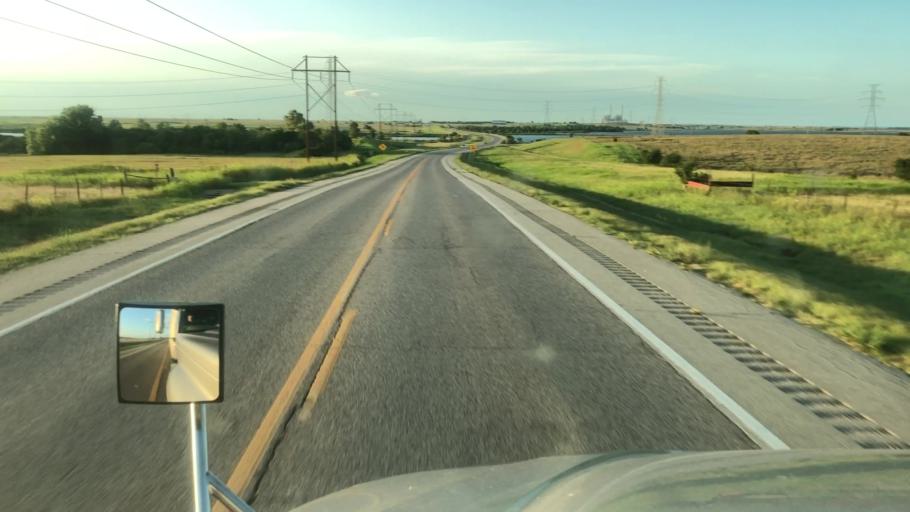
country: US
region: Oklahoma
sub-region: Noble County
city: Perry
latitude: 36.3980
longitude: -97.0676
